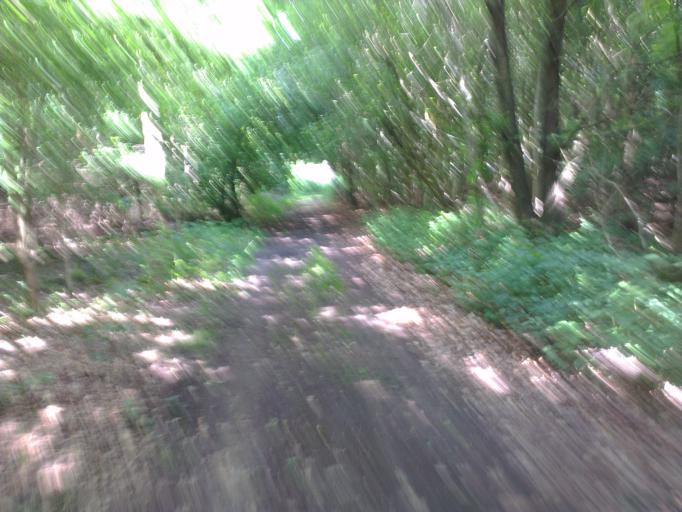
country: DK
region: Capital Region
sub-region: Frederikssund Kommune
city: Jaegerspris
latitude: 55.8170
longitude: 11.9360
